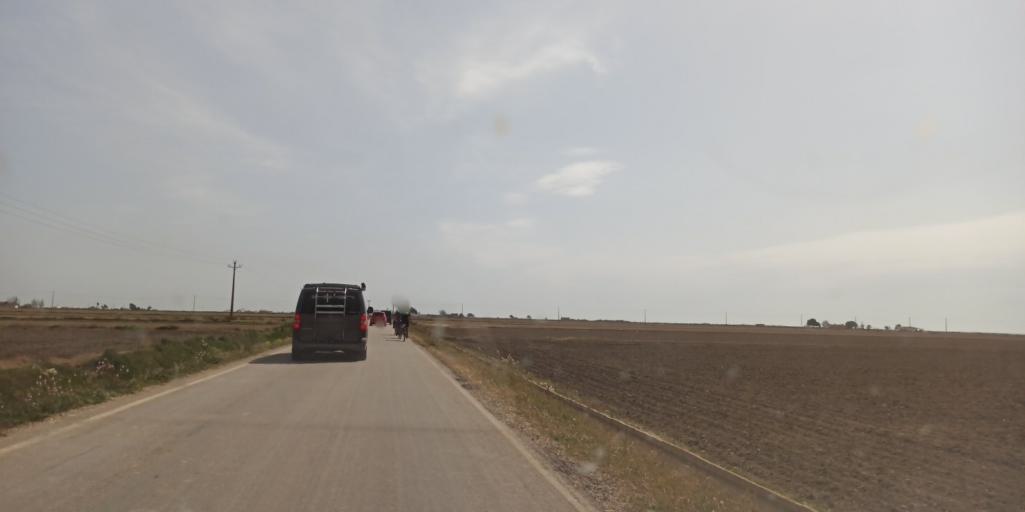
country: ES
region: Catalonia
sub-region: Provincia de Tarragona
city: Deltebre
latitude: 40.6458
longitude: 0.7189
